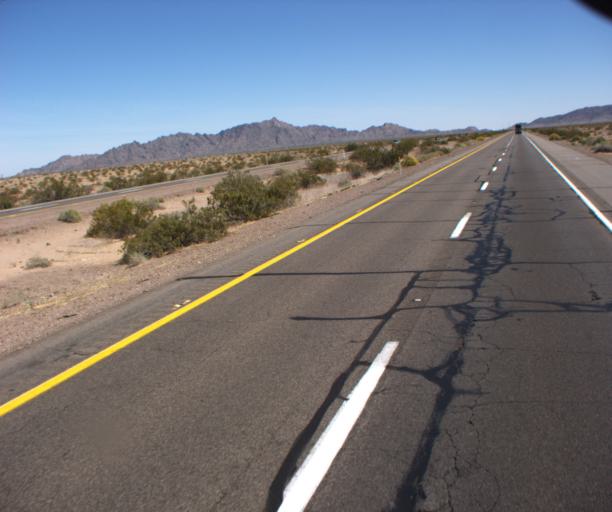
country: US
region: Arizona
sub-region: Yuma County
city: Wellton
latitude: 32.7108
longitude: -113.8385
